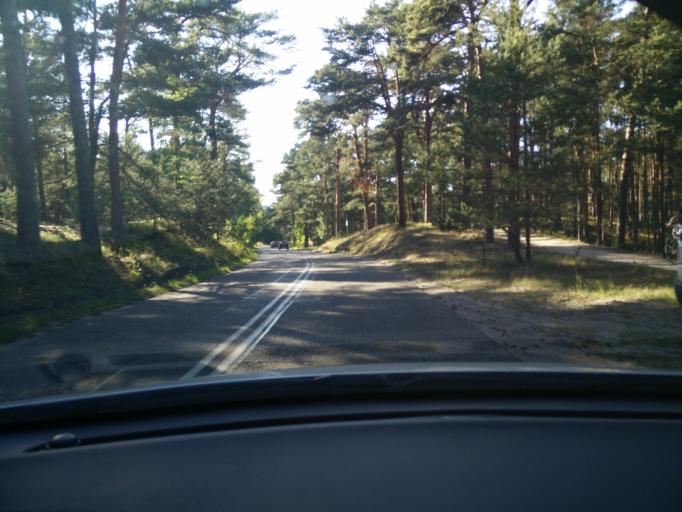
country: PL
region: Pomeranian Voivodeship
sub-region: Powiat pucki
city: Hel
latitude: 54.6497
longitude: 18.7629
